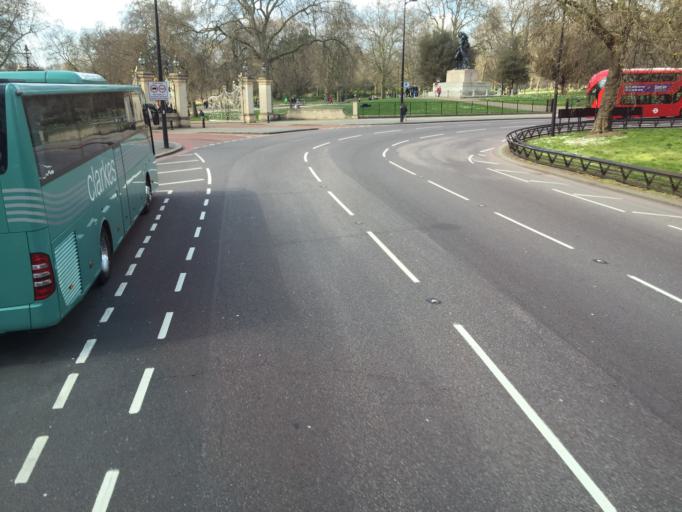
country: GB
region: England
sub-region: Greater London
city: Chelsea
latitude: 51.5040
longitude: -0.1515
